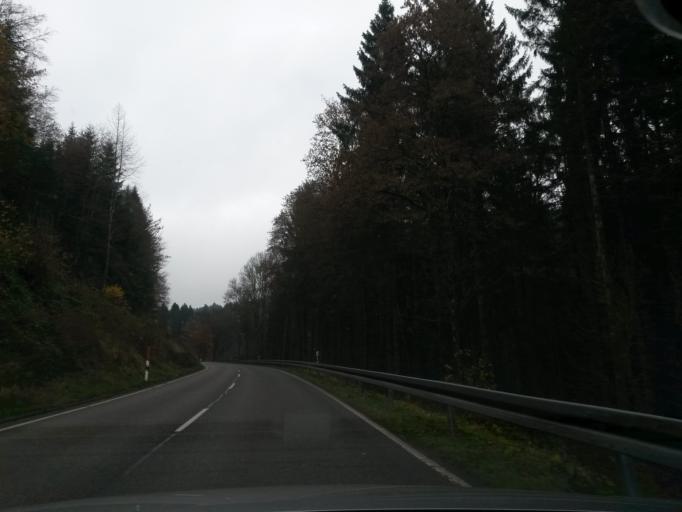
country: DE
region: Baden-Wuerttemberg
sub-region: Karlsruhe Region
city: Alpirsbach
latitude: 48.3418
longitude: 8.4400
